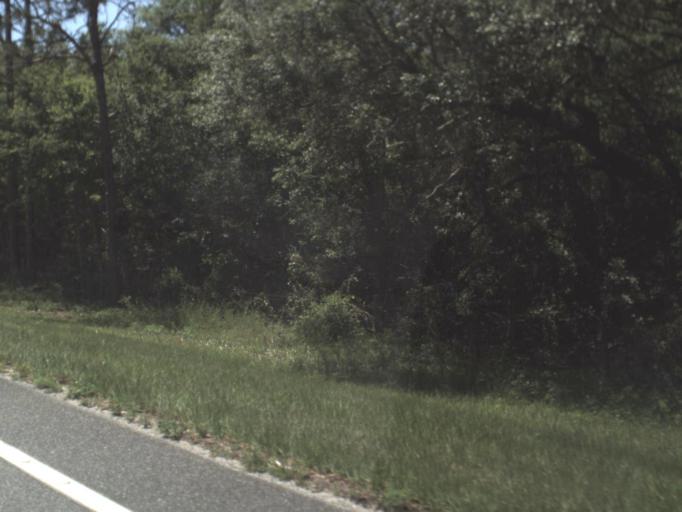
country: US
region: Florida
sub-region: Lafayette County
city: Mayo
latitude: 30.1294
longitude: -83.3221
